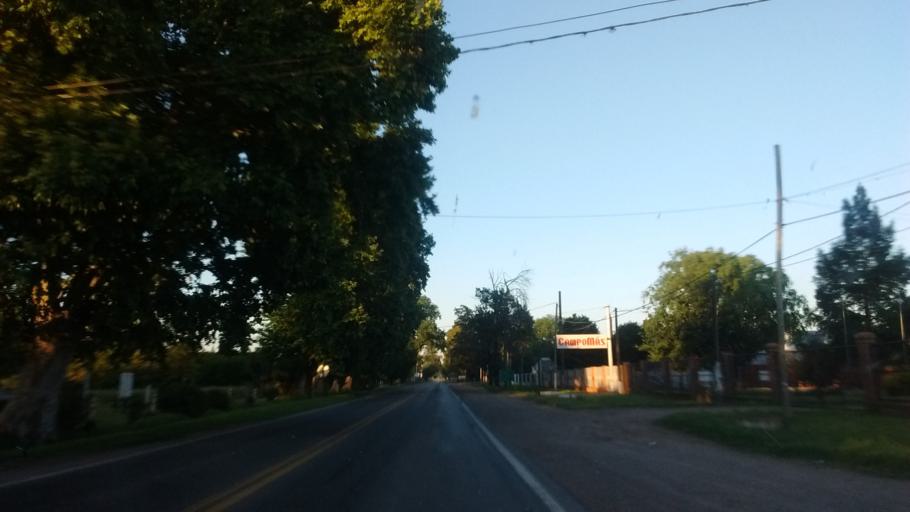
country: AR
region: Santa Fe
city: Casilda
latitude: -33.0645
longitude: -61.1780
